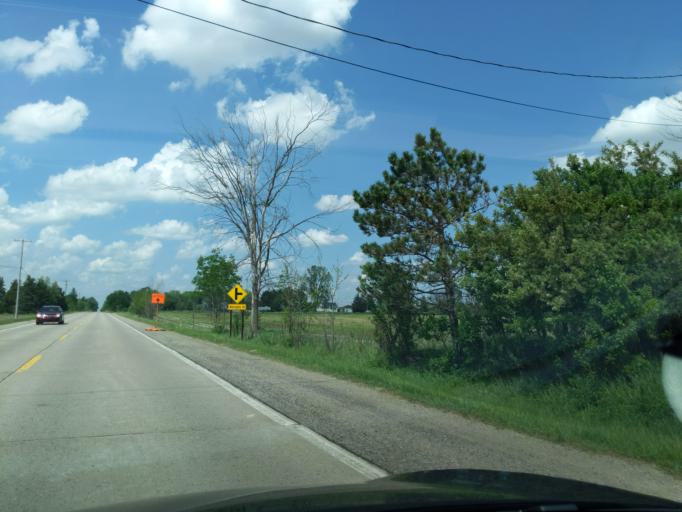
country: US
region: Michigan
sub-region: Ingham County
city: Mason
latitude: 42.6491
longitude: -84.4329
